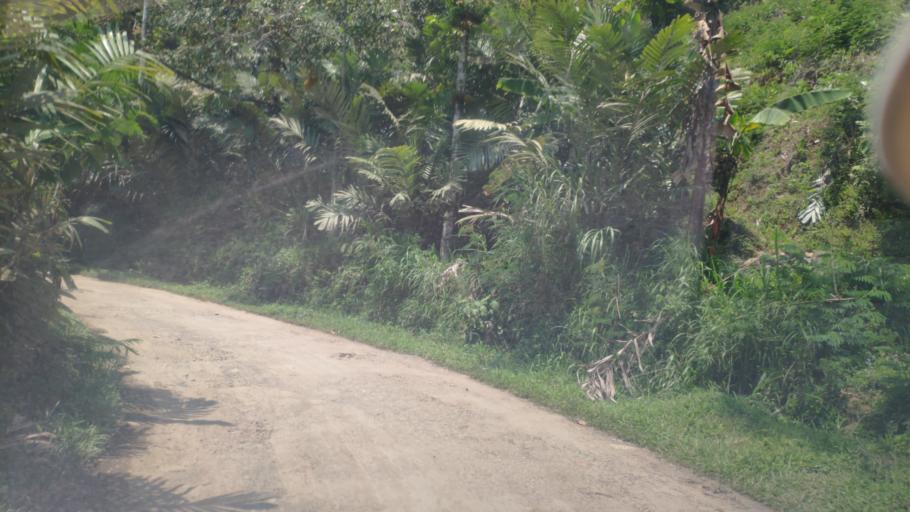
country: ID
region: Central Java
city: Wonosobo
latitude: -7.2831
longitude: 109.7358
